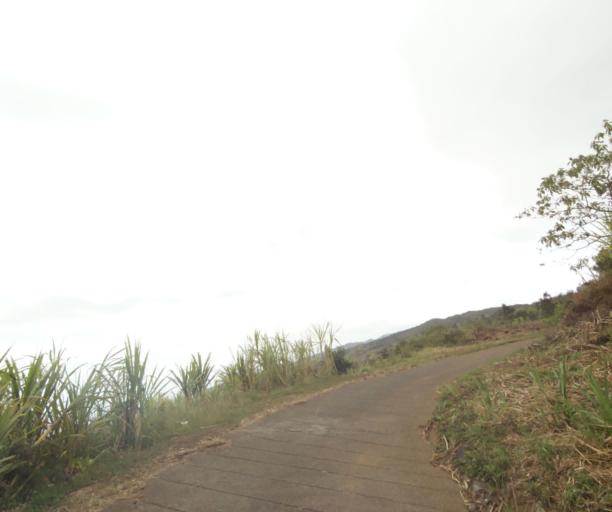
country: RE
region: Reunion
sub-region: Reunion
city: Saint-Paul
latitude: -21.0061
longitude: 55.3489
